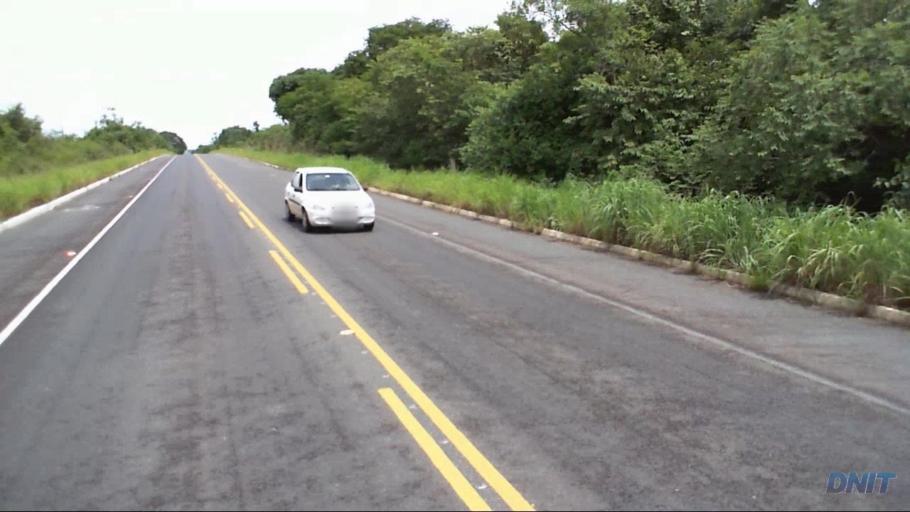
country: BR
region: Goias
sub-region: Sao Miguel Do Araguaia
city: Sao Miguel do Araguaia
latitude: -13.2966
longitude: -50.2408
